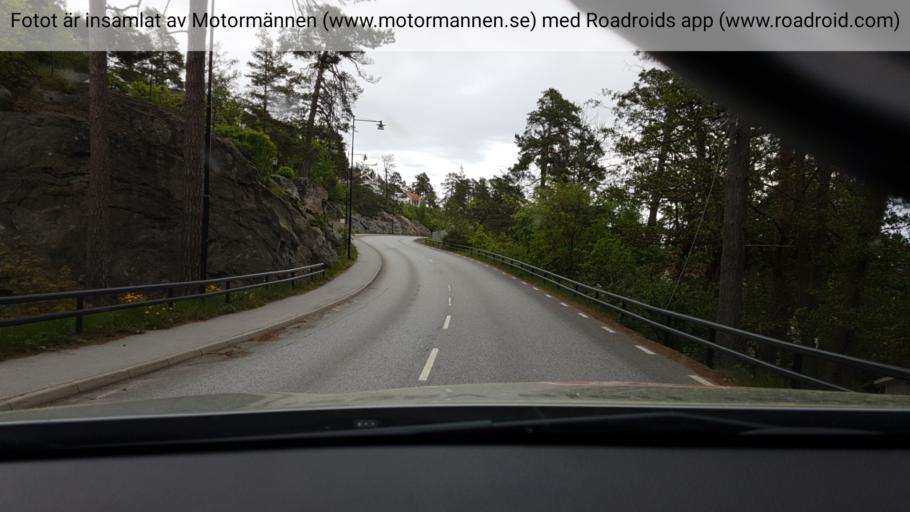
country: SE
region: Stockholm
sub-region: Nacka Kommun
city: Saltsjobaden
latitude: 59.2588
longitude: 18.3326
